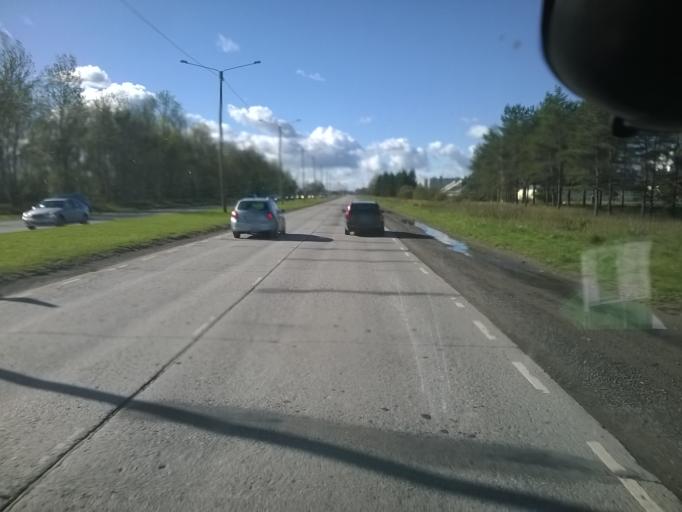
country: EE
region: Harju
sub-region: Tallinna linn
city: Kose
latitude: 59.4407
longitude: 24.8951
